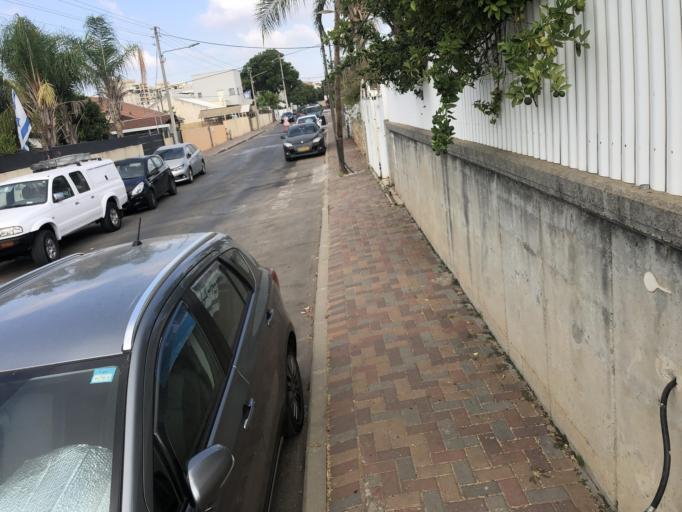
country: IL
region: Central District
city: Yehud
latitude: 32.0362
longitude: 34.8854
